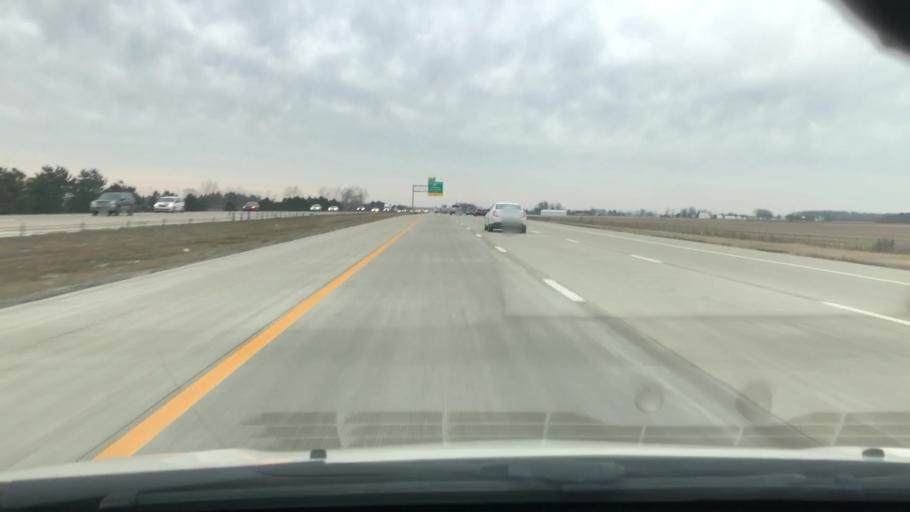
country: US
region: Ohio
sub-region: Wood County
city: Perrysburg
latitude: 41.4955
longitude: -83.6214
